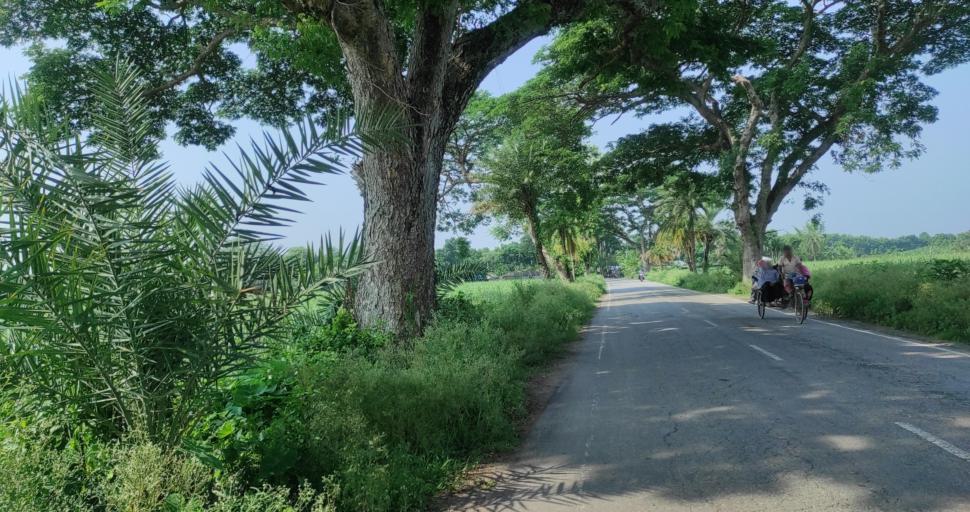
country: BD
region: Rajshahi
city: Ishurdi
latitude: 24.2635
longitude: 89.0501
